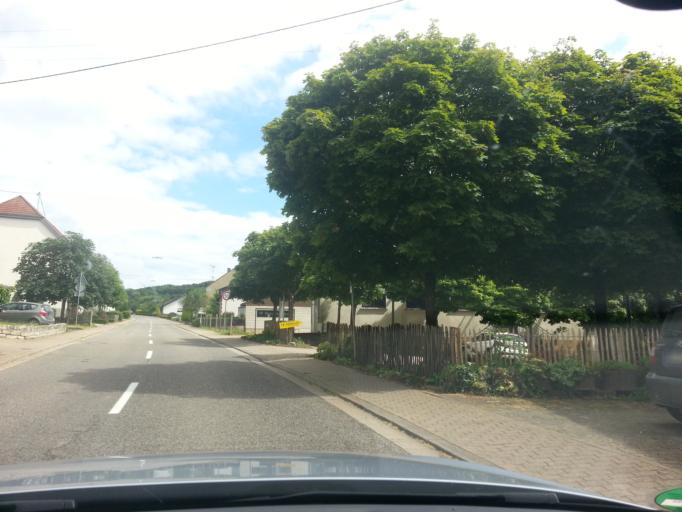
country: DE
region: Saarland
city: Beckingen
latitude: 49.4393
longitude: 6.6821
